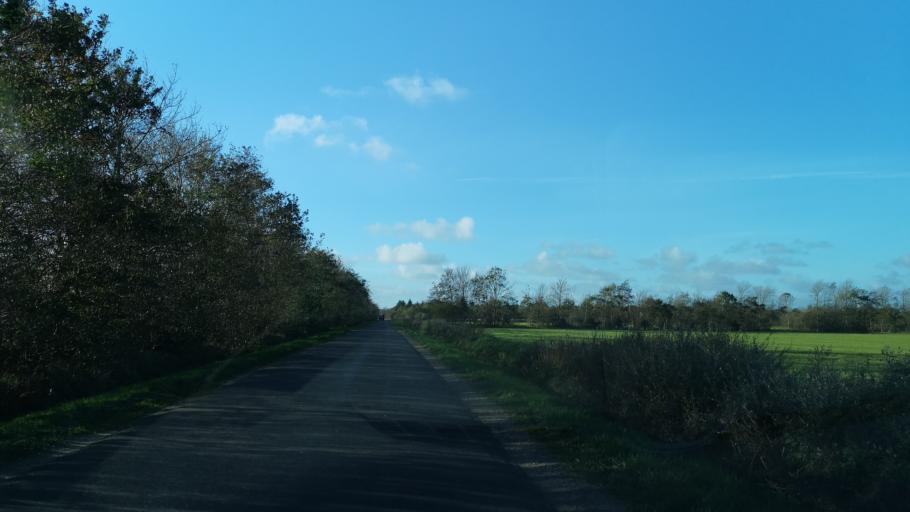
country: DK
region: Central Jutland
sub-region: Ringkobing-Skjern Kommune
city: Tarm
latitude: 55.8254
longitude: 8.3995
